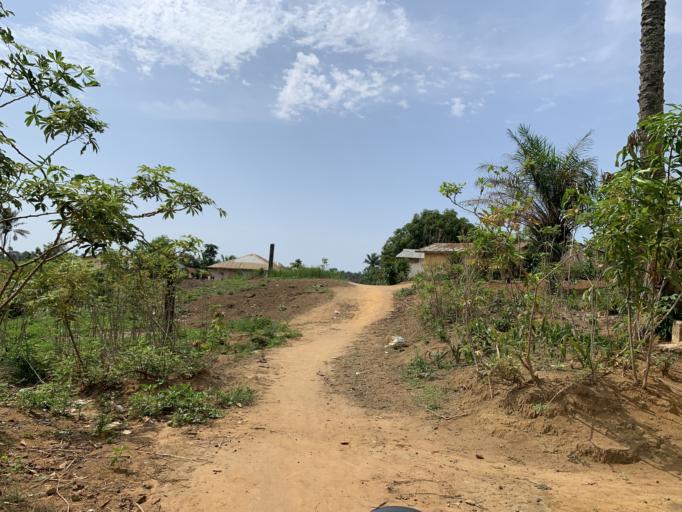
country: SL
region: Western Area
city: Waterloo
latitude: 8.3485
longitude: -13.0529
